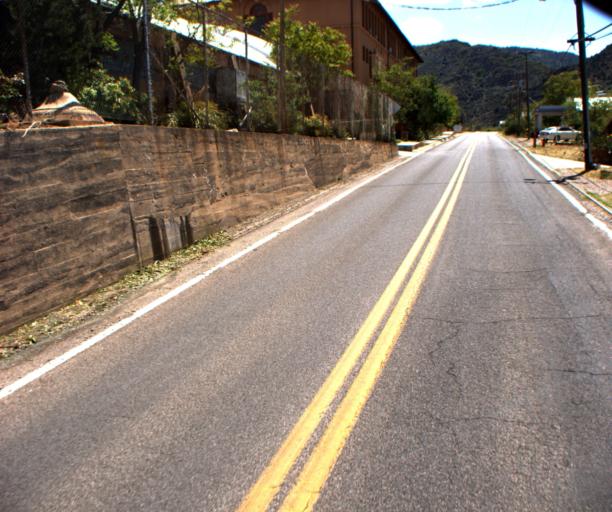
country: US
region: Arizona
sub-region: Yavapai County
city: Clarkdale
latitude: 34.7517
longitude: -112.1054
